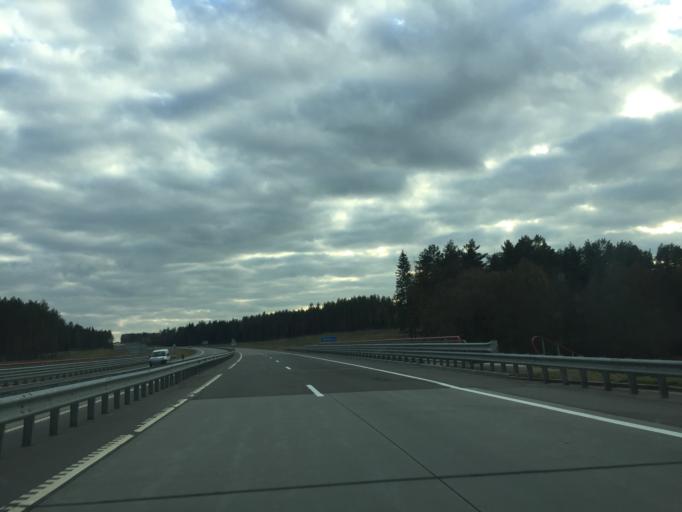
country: BY
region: Minsk
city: Rakaw
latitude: 53.9566
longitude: 27.0802
